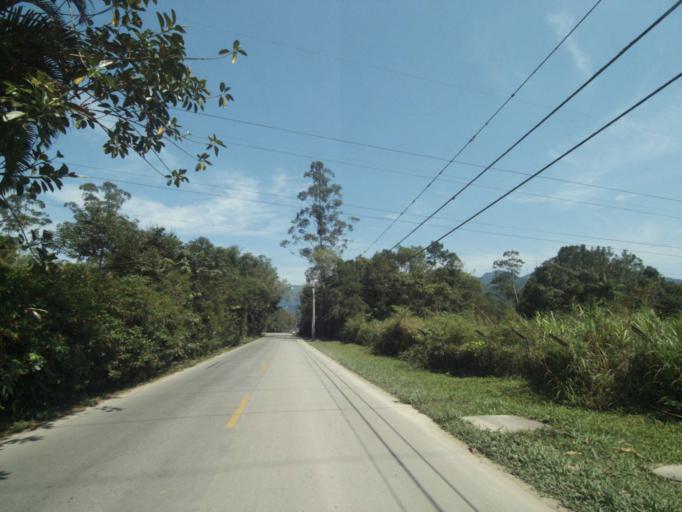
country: BR
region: Parana
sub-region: Paranagua
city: Paranagua
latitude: -25.5620
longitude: -48.6267
